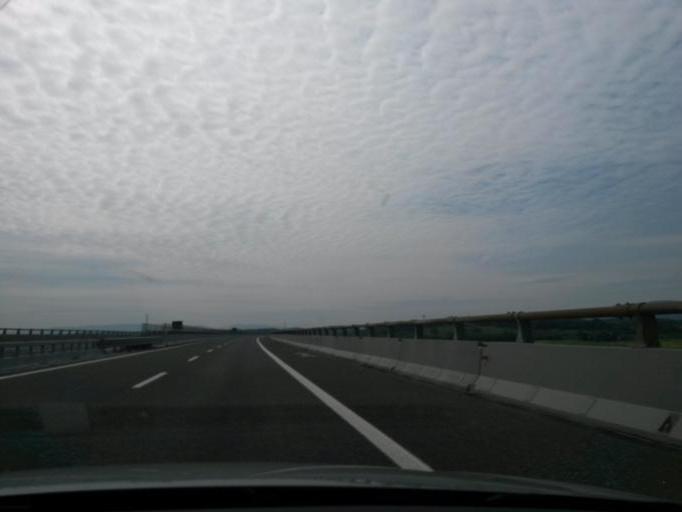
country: IT
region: Tuscany
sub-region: Provincia di Livorno
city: Vicarello
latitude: 43.6089
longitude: 10.4440
